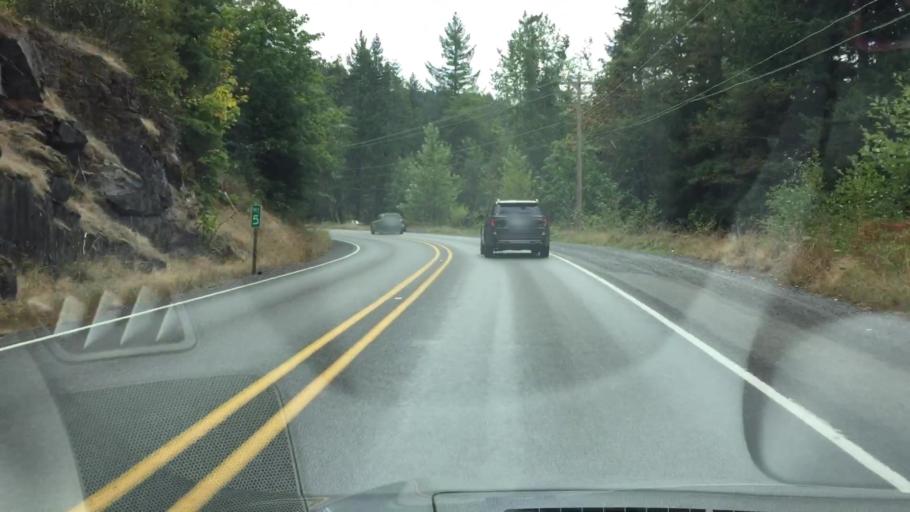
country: US
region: Washington
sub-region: Pierce County
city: Eatonville
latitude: 46.8495
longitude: -122.2708
